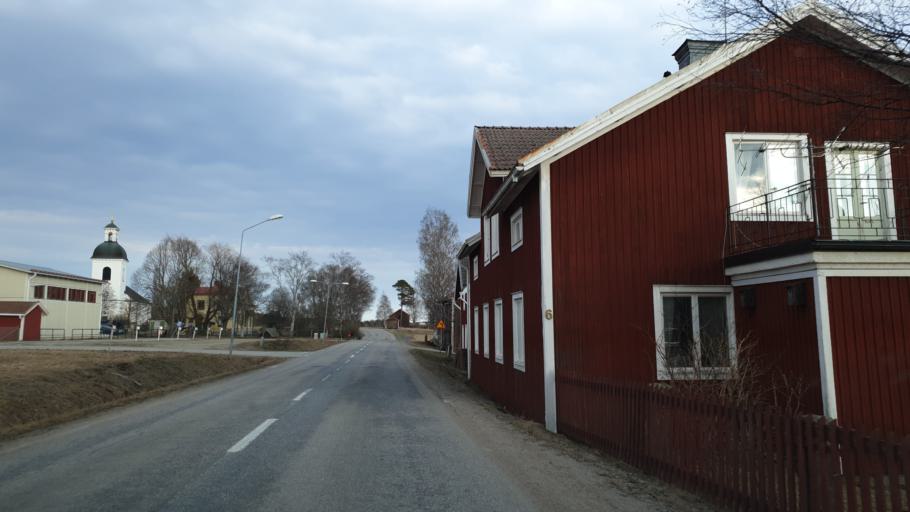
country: SE
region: Gaevleborg
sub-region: Nordanstigs Kommun
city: Bergsjoe
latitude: 61.9739
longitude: 17.2546
